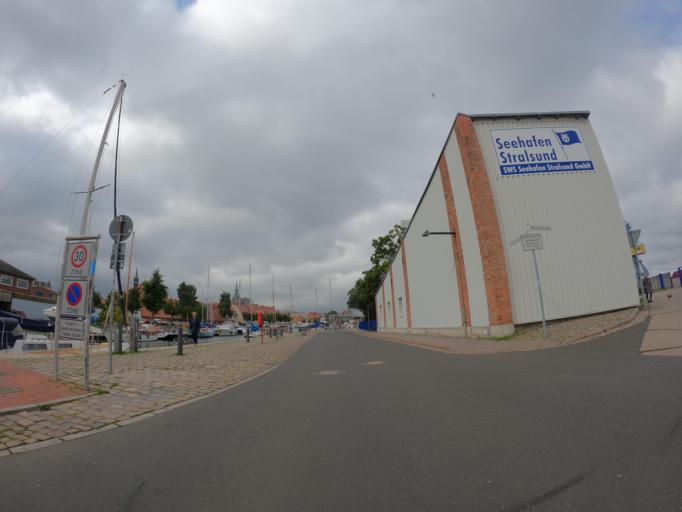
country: DE
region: Mecklenburg-Vorpommern
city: Stralsund
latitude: 54.3124
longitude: 13.0998
